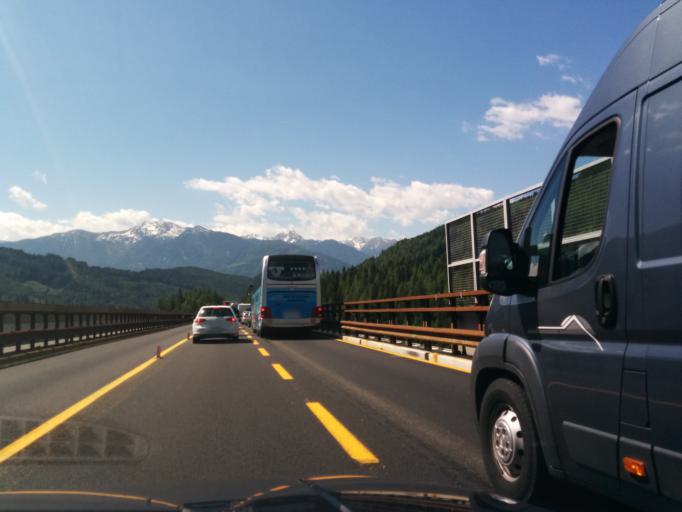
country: IT
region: Trentino-Alto Adige
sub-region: Bolzano
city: Brennero - Brenner
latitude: 46.9324
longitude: 11.4477
